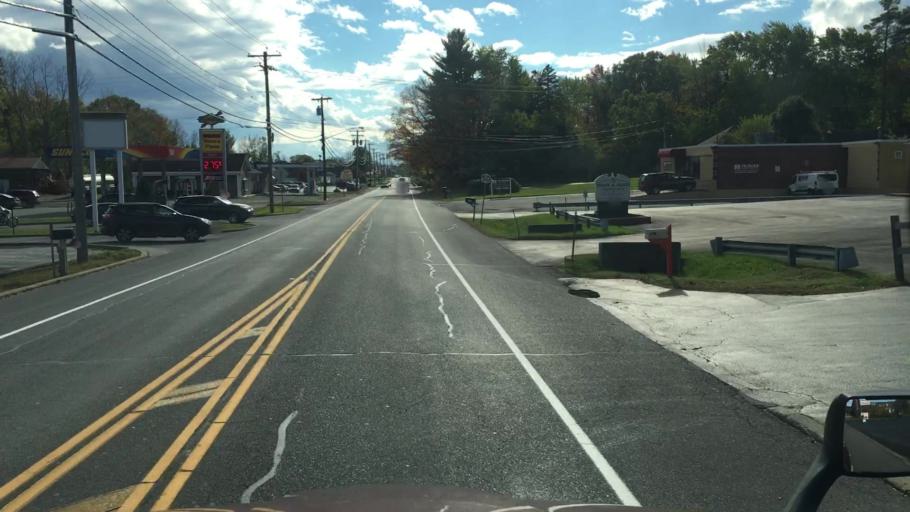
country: US
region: New York
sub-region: Schenectady County
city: East Glenville
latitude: 42.9094
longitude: -73.8991
